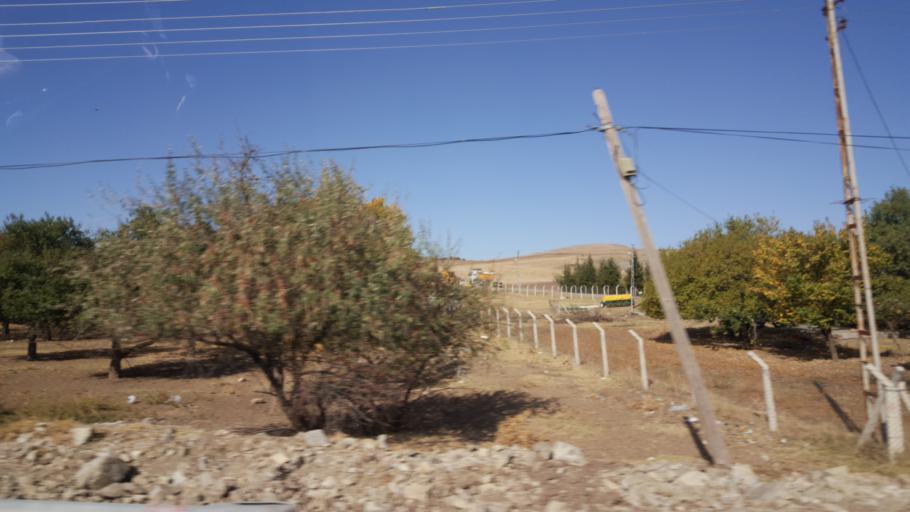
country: TR
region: Ankara
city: Ikizce
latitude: 39.5404
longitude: 32.6251
